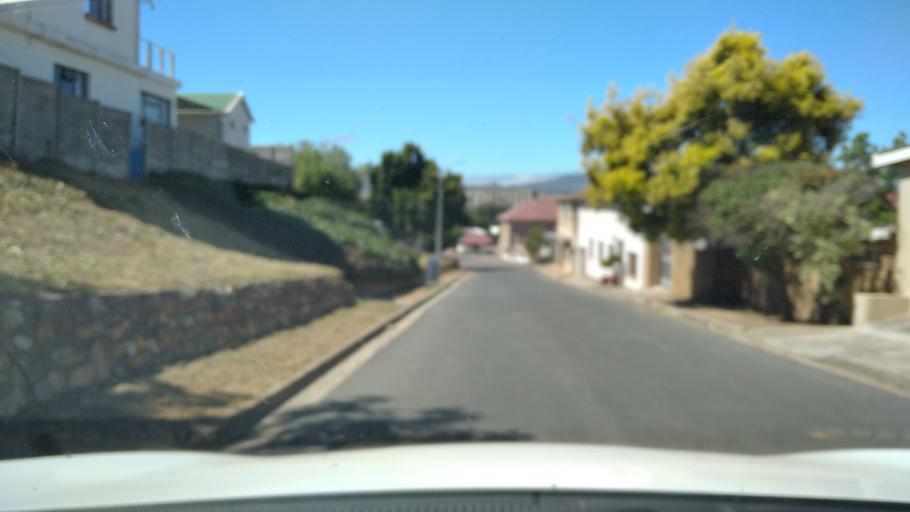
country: ZA
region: Western Cape
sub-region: Overberg District Municipality
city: Caledon
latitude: -34.2301
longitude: 19.4304
